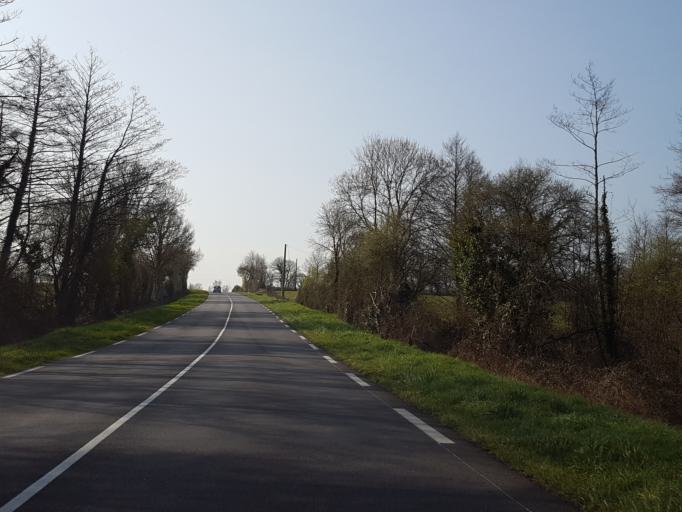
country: FR
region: Pays de la Loire
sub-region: Departement de la Vendee
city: Rocheserviere
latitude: 46.9153
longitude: -1.5060
